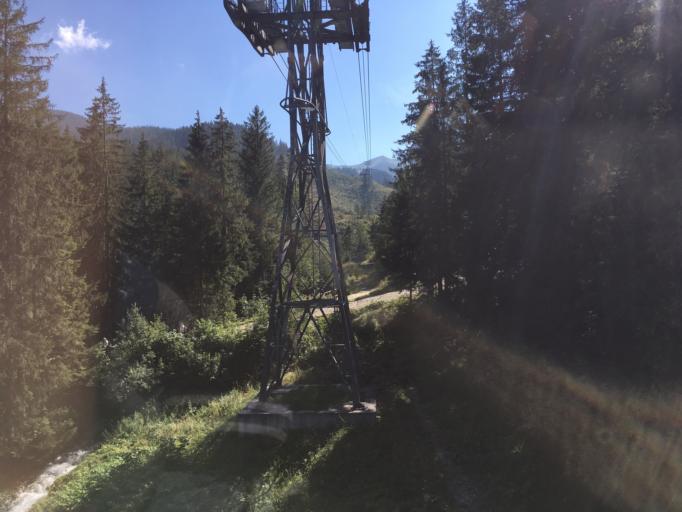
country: PL
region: Lesser Poland Voivodeship
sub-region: Powiat tatrzanski
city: Zakopane
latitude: 49.2684
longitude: 19.9788
